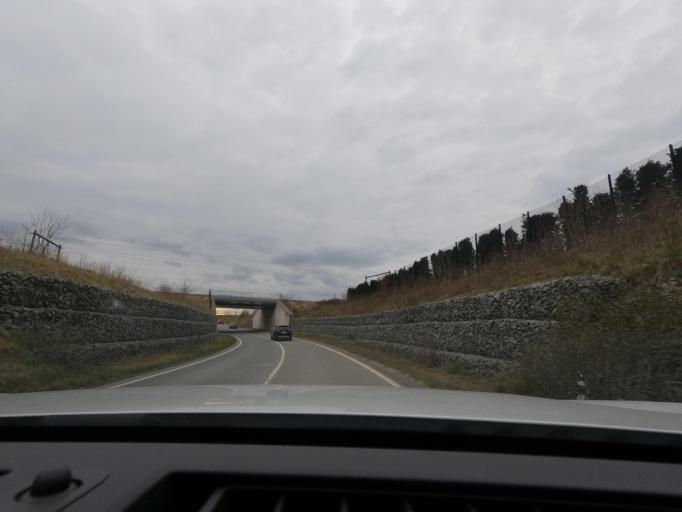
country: BE
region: Wallonia
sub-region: Province du Hainaut
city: Lens
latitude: 50.5809
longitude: 3.8834
